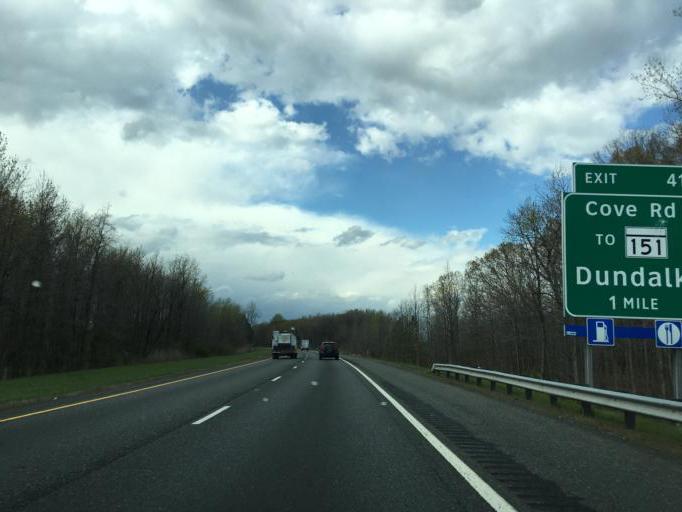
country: US
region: Maryland
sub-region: Baltimore County
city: Edgemere
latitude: 39.2638
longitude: -76.4587
